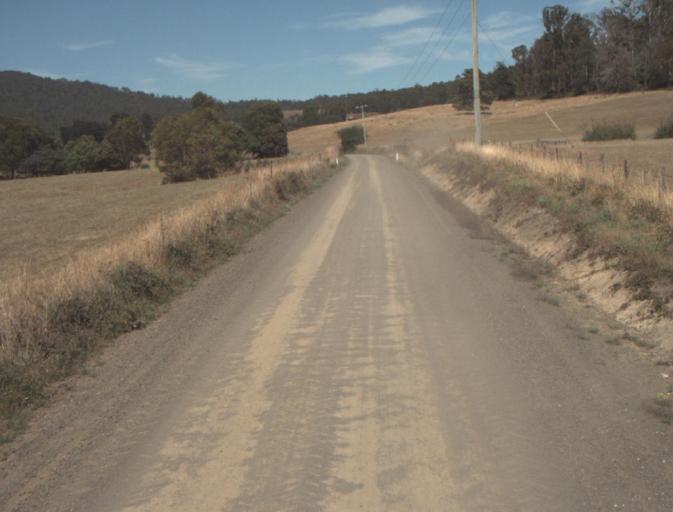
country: AU
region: Tasmania
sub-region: Launceston
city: Mayfield
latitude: -41.2545
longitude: 147.1331
